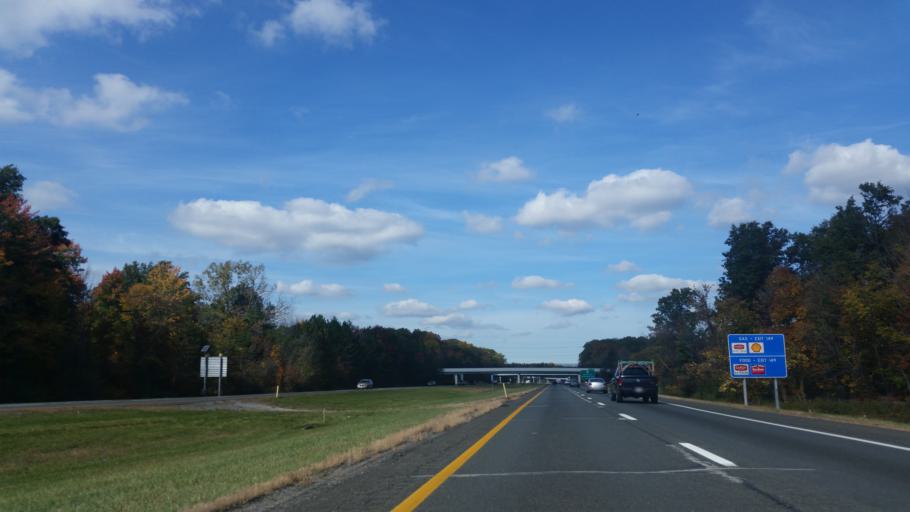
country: US
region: Ohio
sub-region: Cuyahoga County
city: Brecksville
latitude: 41.2971
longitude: -81.6413
